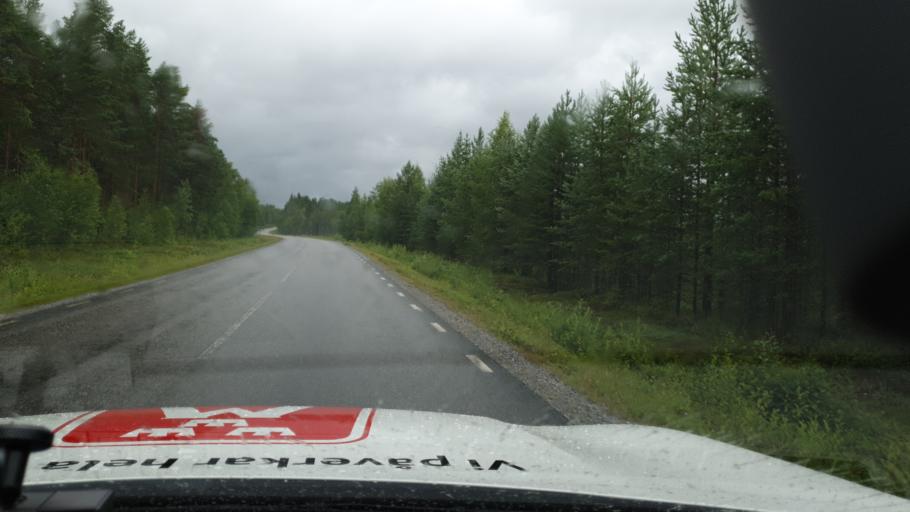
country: SE
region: Norrbotten
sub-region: Pitea Kommun
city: Roknas
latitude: 65.3524
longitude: 21.0947
